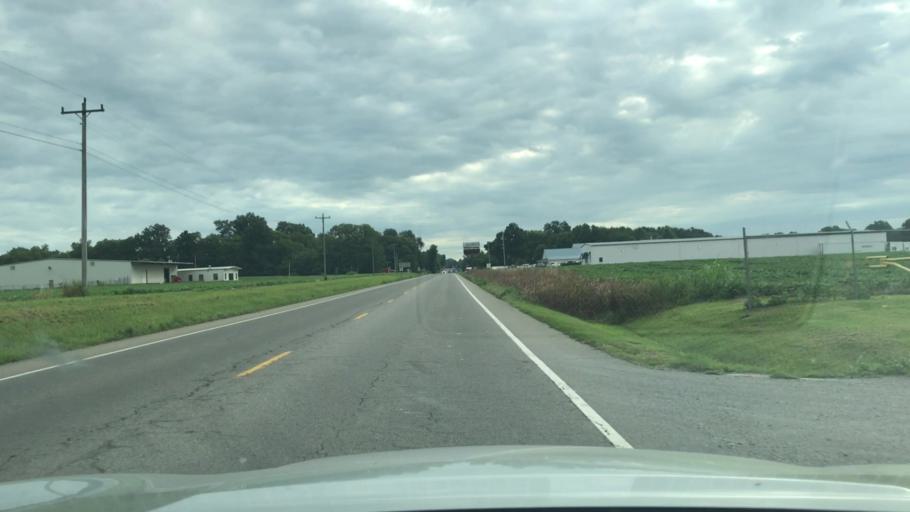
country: US
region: Kentucky
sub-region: Todd County
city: Guthrie
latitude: 36.6385
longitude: -87.2080
